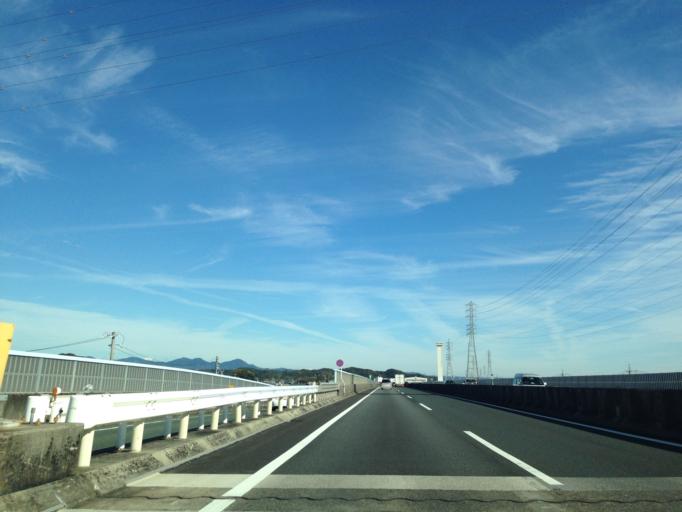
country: JP
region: Shizuoka
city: Fukuroi
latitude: 34.7561
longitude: 137.9188
